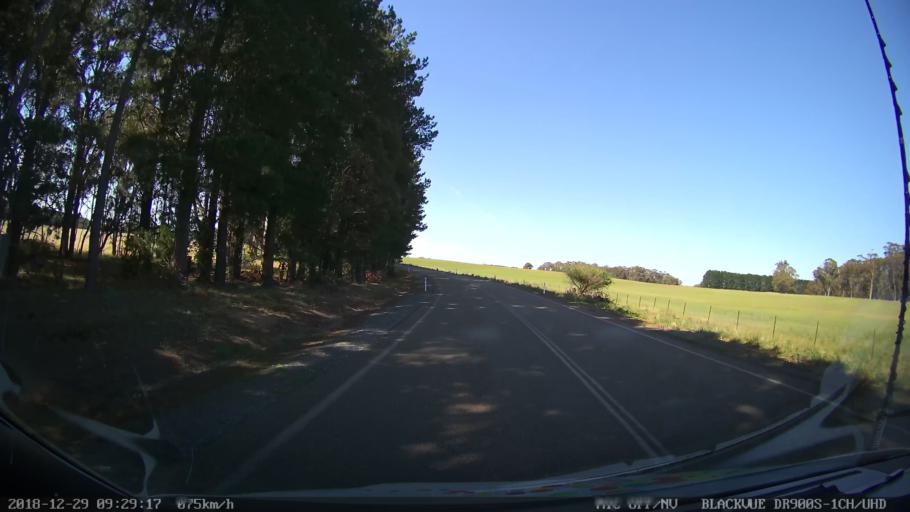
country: AU
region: New South Wales
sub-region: Upper Lachlan Shire
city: Crookwell
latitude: -34.5862
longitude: 149.3757
